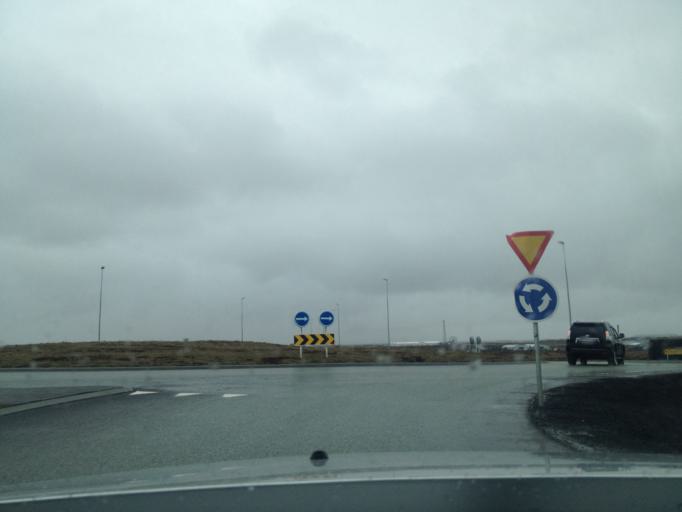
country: IS
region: Southern Peninsula
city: Reykjanesbaer
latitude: 63.9900
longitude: -22.5778
